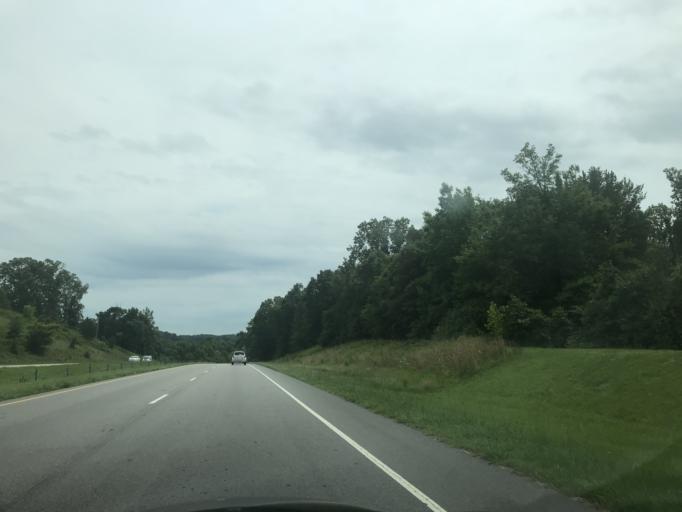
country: US
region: North Carolina
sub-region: Franklin County
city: Franklinton
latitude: 36.1755
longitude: -78.4474
